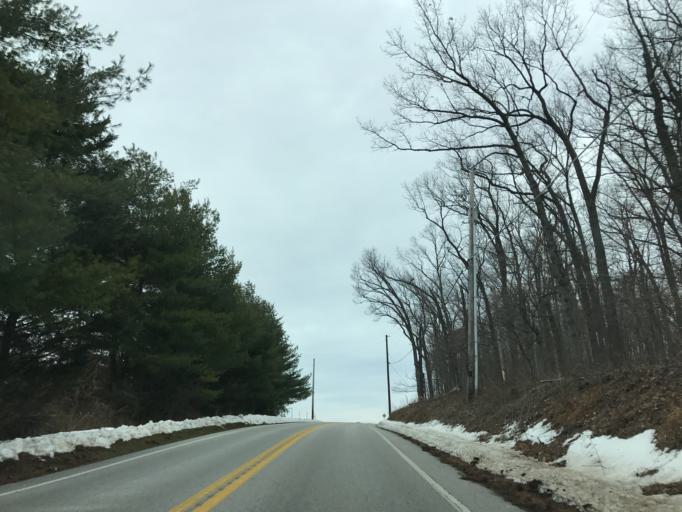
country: US
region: Pennsylvania
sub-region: York County
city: New Freedom
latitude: 39.7289
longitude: -76.7174
